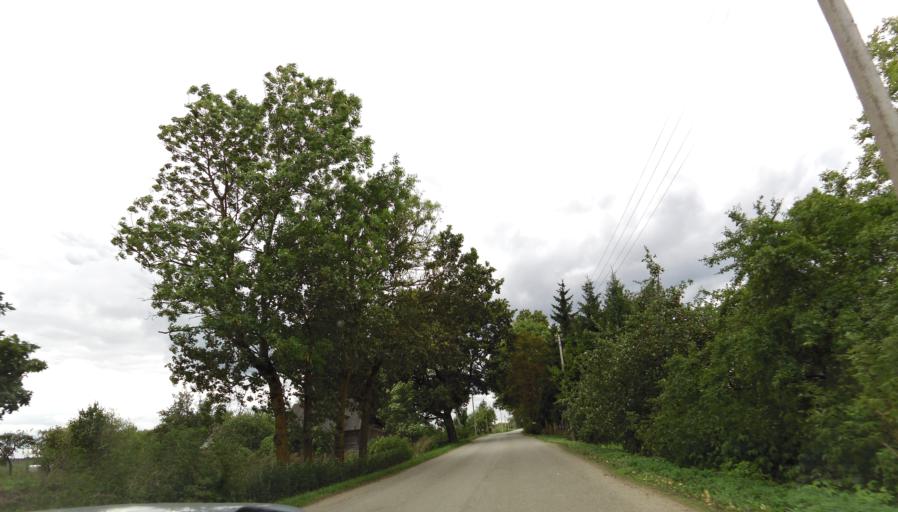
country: LT
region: Panevezys
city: Pasvalys
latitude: 56.0768
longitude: 24.3139
